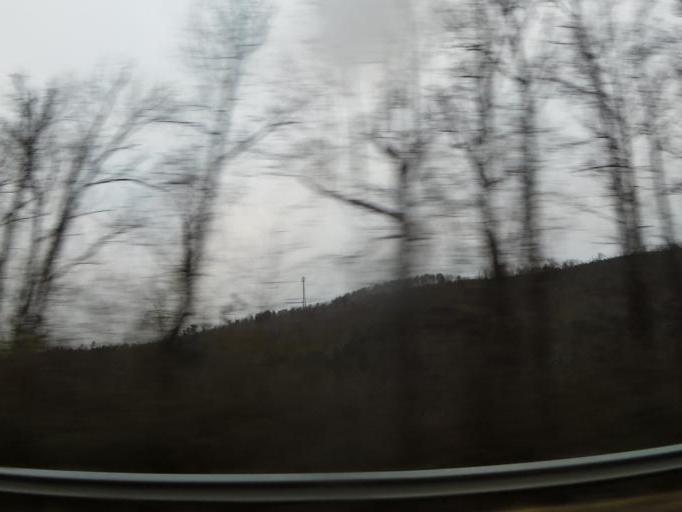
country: US
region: Alabama
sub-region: Cullman County
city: Good Hope
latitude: 34.0094
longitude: -86.8638
